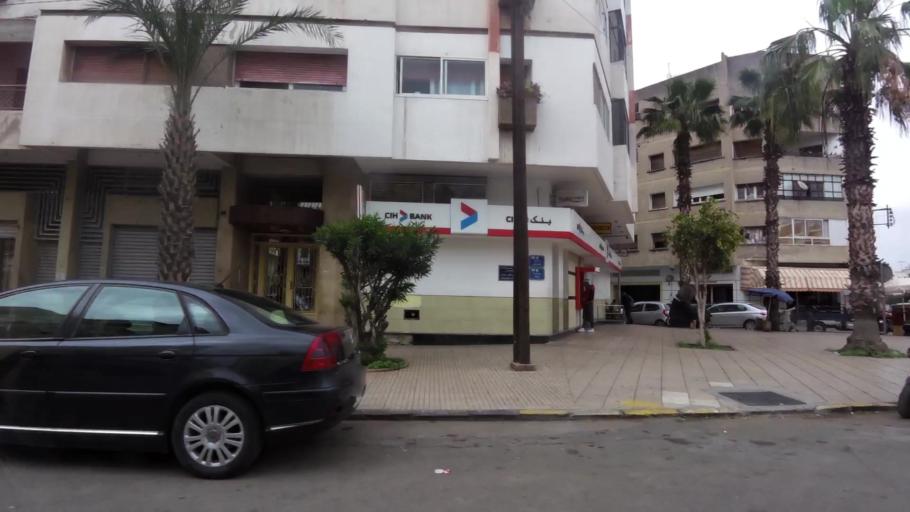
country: MA
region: Grand Casablanca
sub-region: Casablanca
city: Casablanca
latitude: 33.5986
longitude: -7.6450
